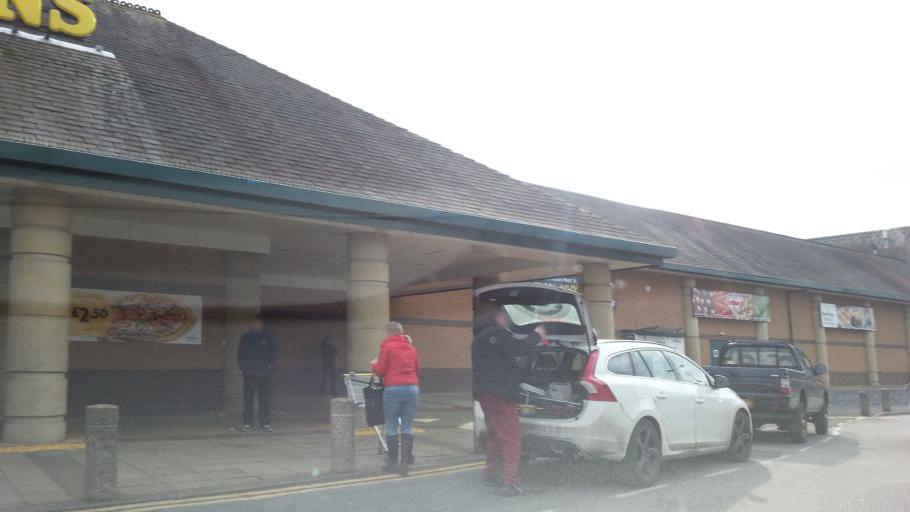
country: GB
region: England
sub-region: Northamptonshire
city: Corby
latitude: 52.4715
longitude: -0.7199
